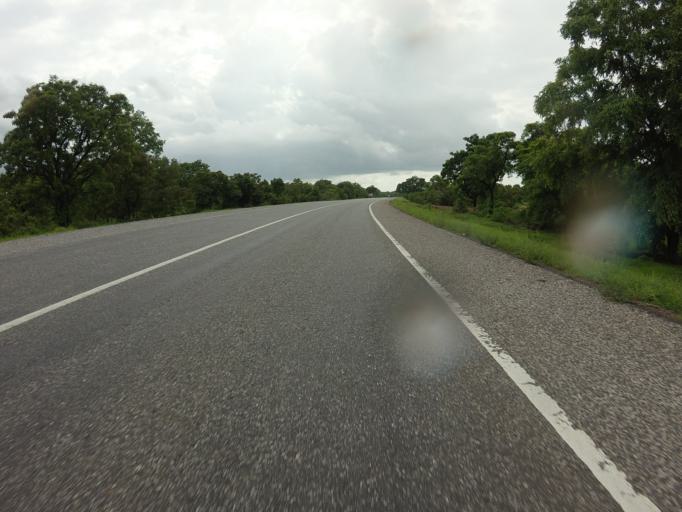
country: GH
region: Northern
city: Tamale
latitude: 9.1369
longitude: -1.3456
